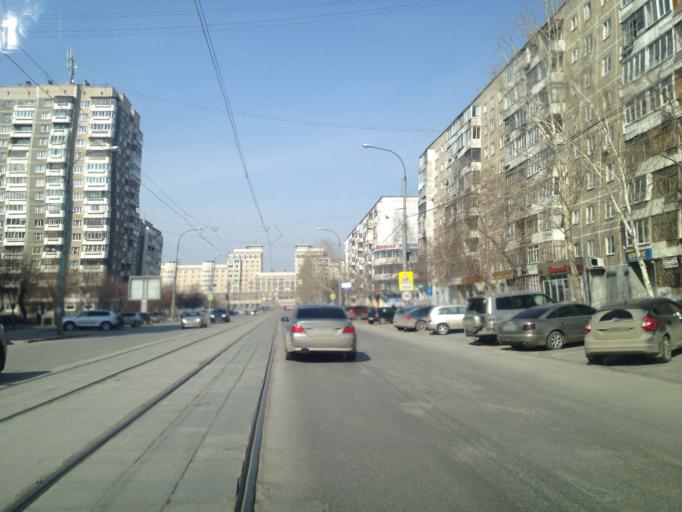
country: RU
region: Sverdlovsk
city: Shirokaya Rechka
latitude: 56.8326
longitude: 60.5451
